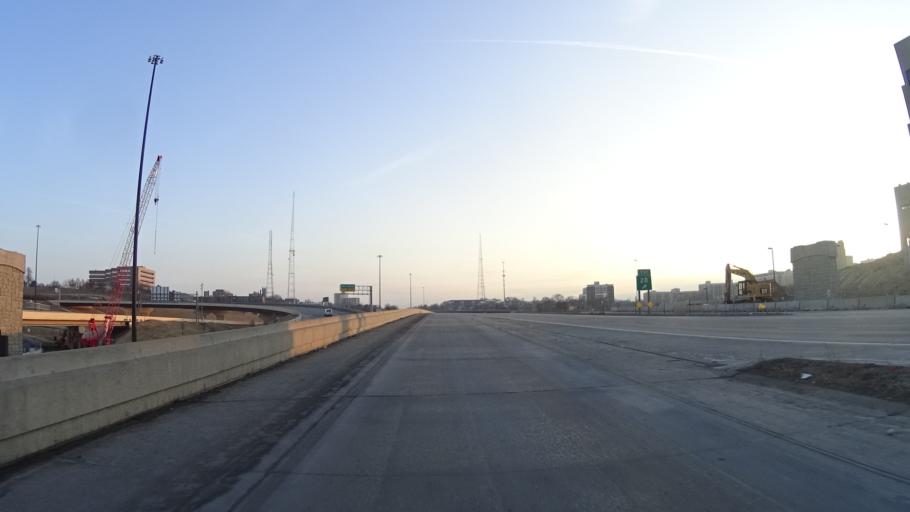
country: US
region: Nebraska
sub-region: Douglas County
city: Omaha
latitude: 41.2652
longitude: -95.9529
